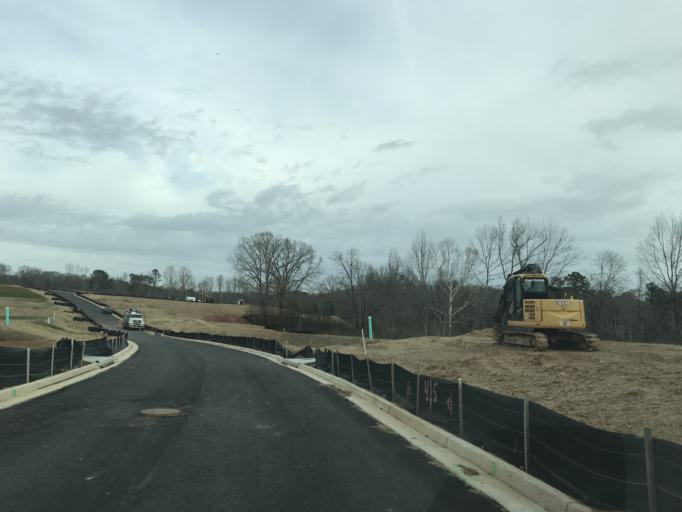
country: US
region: Georgia
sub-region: Cherokee County
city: Canton
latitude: 34.1958
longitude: -84.3978
